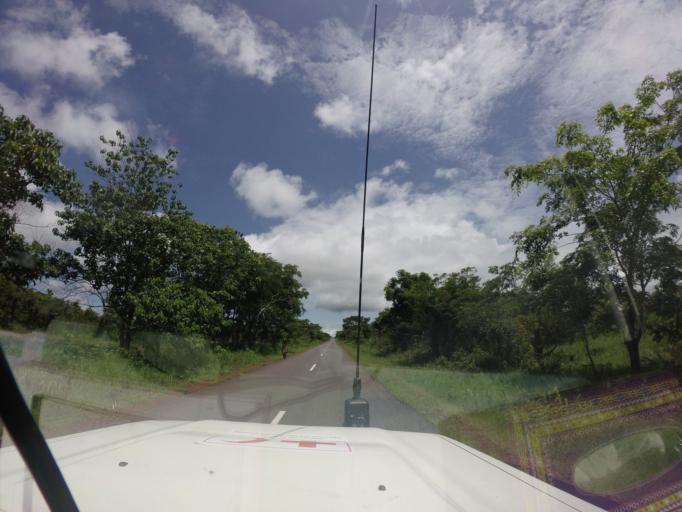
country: GN
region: Faranah
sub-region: Faranah Prefecture
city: Faranah
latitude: 10.0251
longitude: -10.7978
